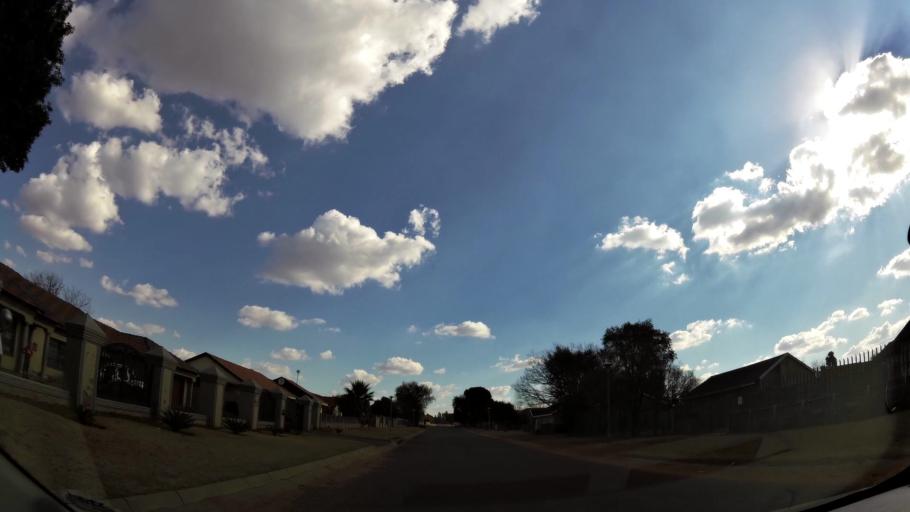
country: ZA
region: Mpumalanga
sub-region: Nkangala District Municipality
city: Witbank
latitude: -25.9241
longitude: 29.2192
